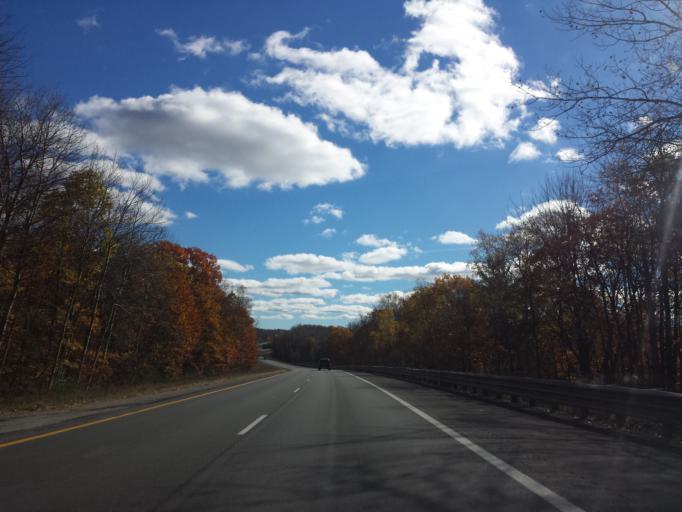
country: US
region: Michigan
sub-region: Cheboygan County
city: Indian River
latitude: 45.3520
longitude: -84.6143
